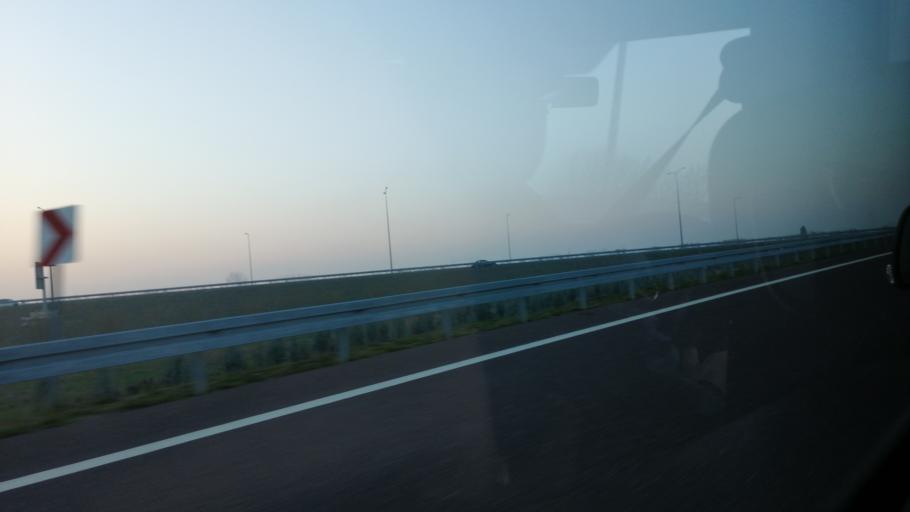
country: TR
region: Yalova
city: Altinova
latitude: 40.6991
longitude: 29.4894
